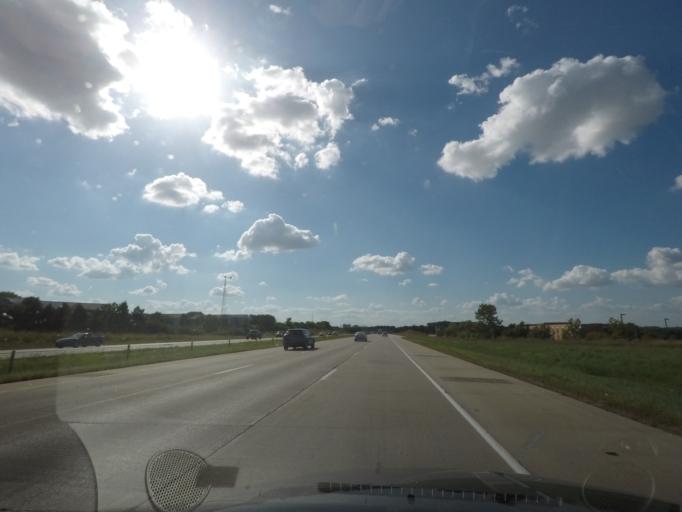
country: US
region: Iowa
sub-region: Polk County
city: Clive
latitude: 41.5923
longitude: -93.7931
